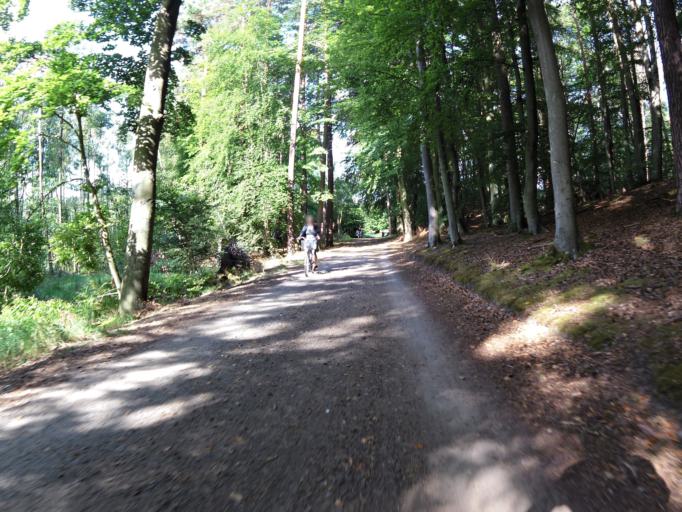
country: DE
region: Mecklenburg-Vorpommern
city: Seebad Bansin
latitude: 53.9892
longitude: 14.1150
